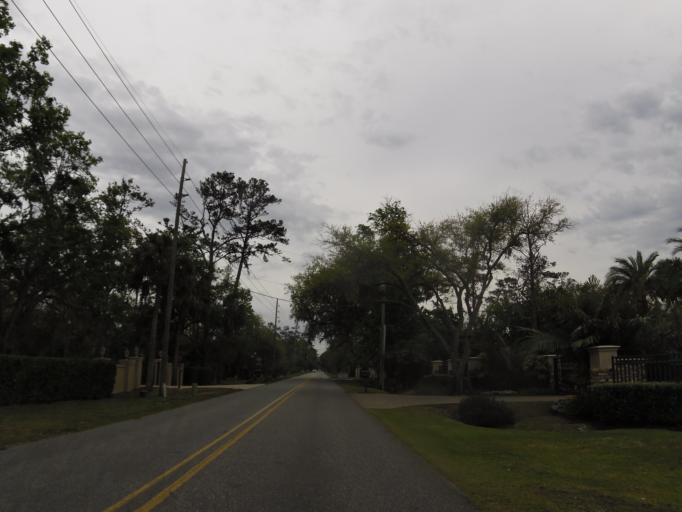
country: US
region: Florida
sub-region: Saint Johns County
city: Palm Valley
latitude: 30.2047
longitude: -81.4073
